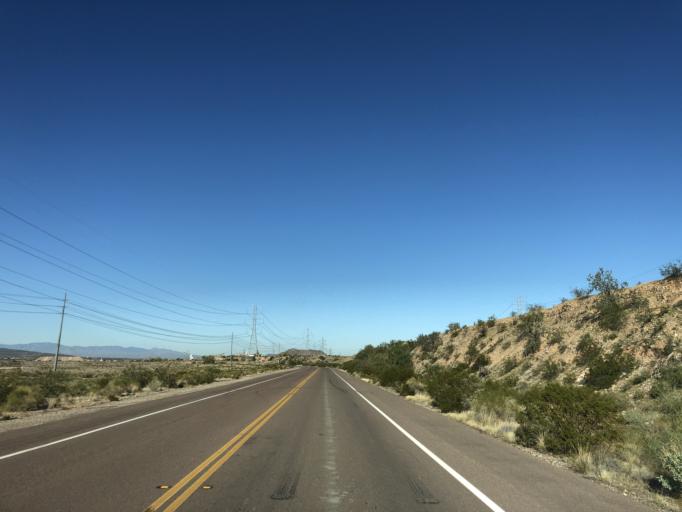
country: US
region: Arizona
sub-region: Maricopa County
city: Sun City West
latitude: 33.6891
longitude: -112.2957
